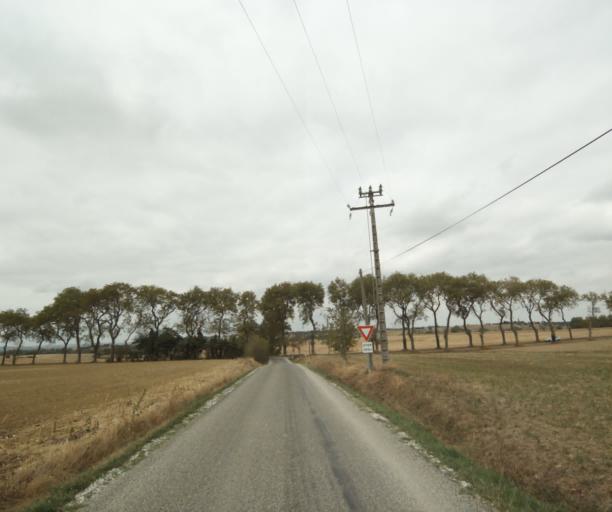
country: FR
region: Midi-Pyrenees
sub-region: Departement de la Haute-Garonne
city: Villefranche-de-Lauragais
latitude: 43.4069
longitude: 1.7317
